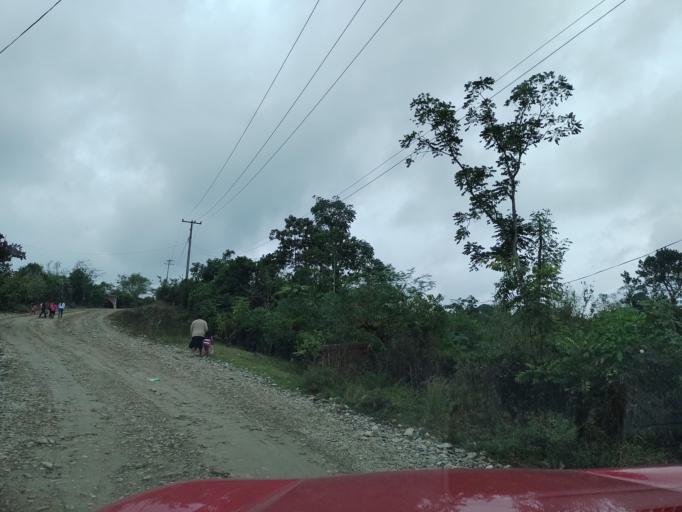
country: MX
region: Veracruz
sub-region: Coatzintla
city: Manuel Maria Contreras
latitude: 20.4082
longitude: -97.4561
